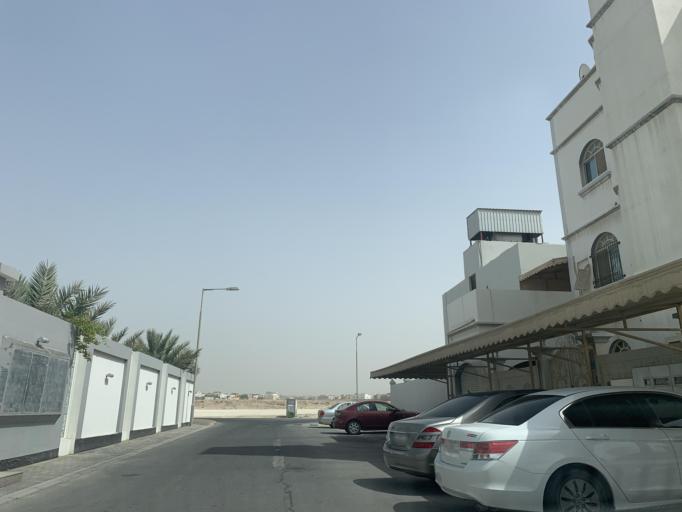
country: BH
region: Central Governorate
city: Madinat Hamad
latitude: 26.1532
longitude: 50.5103
